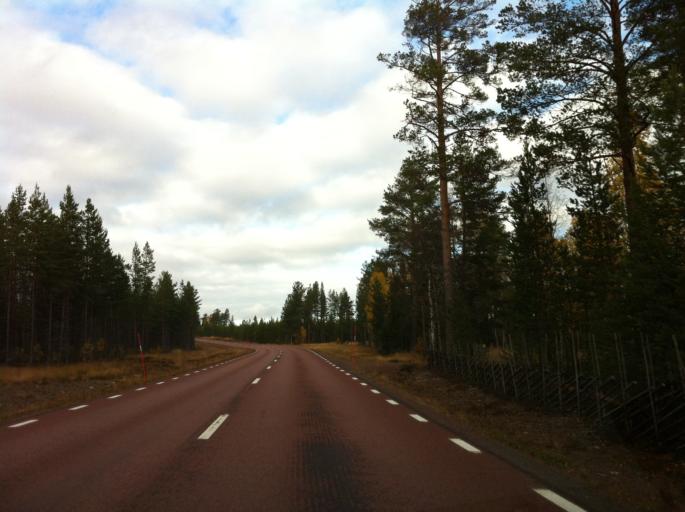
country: SE
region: Dalarna
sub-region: Alvdalens Kommun
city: AElvdalen
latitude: 61.5455
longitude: 13.3364
